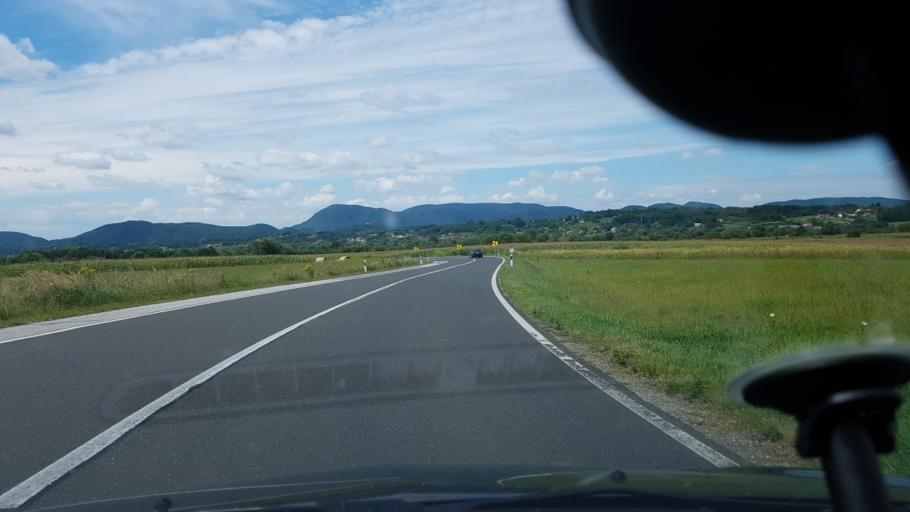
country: HR
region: Varazdinska
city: Ivanec
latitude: 46.2245
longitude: 16.0900
